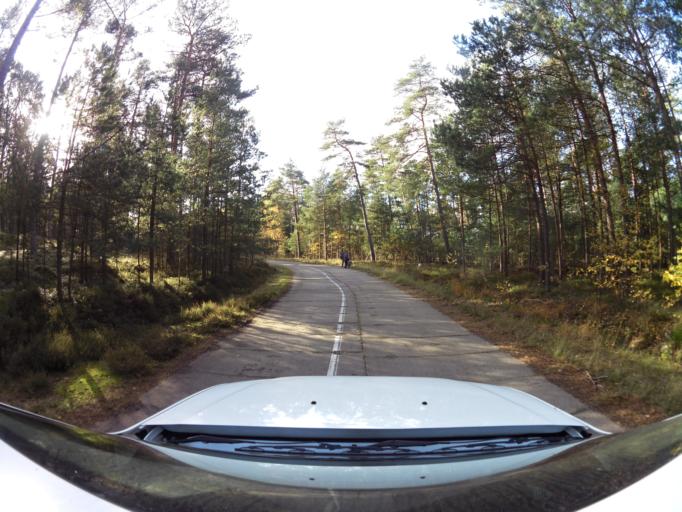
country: PL
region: West Pomeranian Voivodeship
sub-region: Powiat gryficki
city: Cerkwica
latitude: 54.1026
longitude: 15.1428
